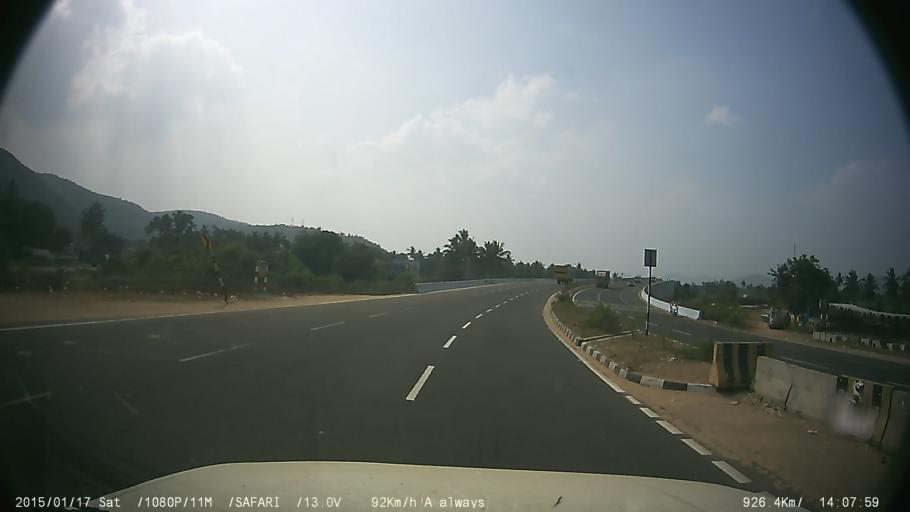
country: IN
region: Tamil Nadu
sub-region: Vellore
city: Ambur
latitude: 12.8251
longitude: 78.7681
